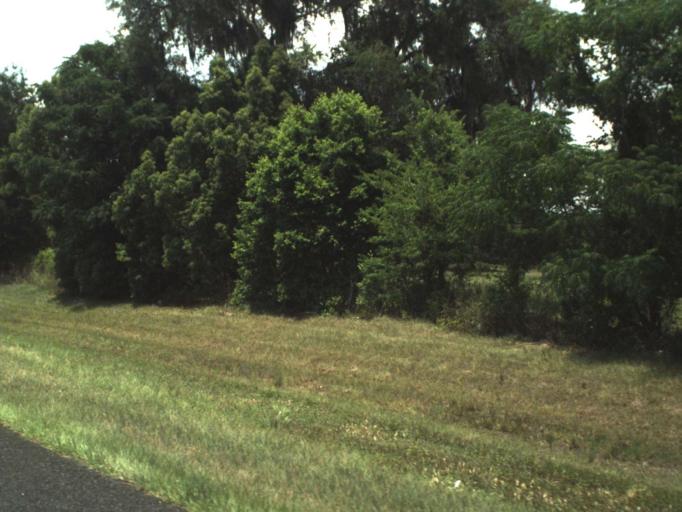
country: US
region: Florida
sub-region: Lake County
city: Fruitland Park
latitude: 28.8142
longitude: -81.9332
